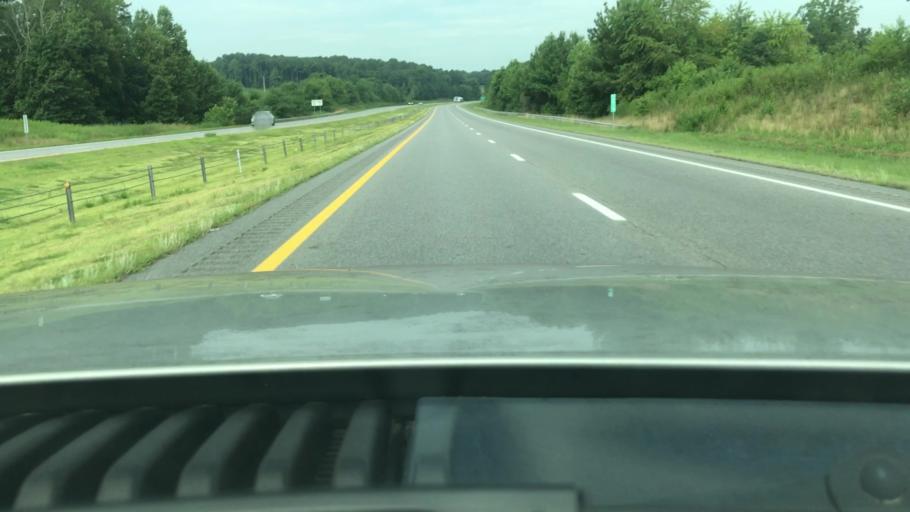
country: US
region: North Carolina
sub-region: Surry County
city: Elkin
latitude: 36.1605
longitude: -80.9598
